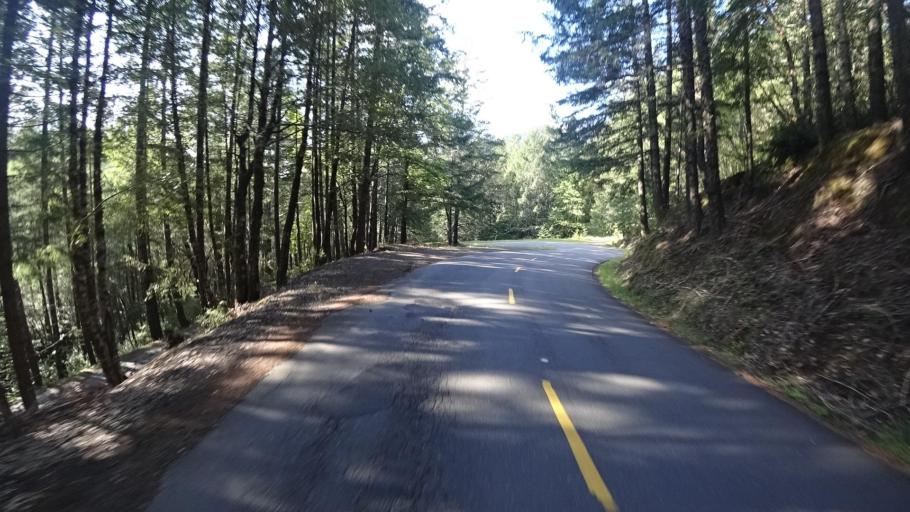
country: US
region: California
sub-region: Humboldt County
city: Rio Dell
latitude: 40.3255
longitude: -124.0458
